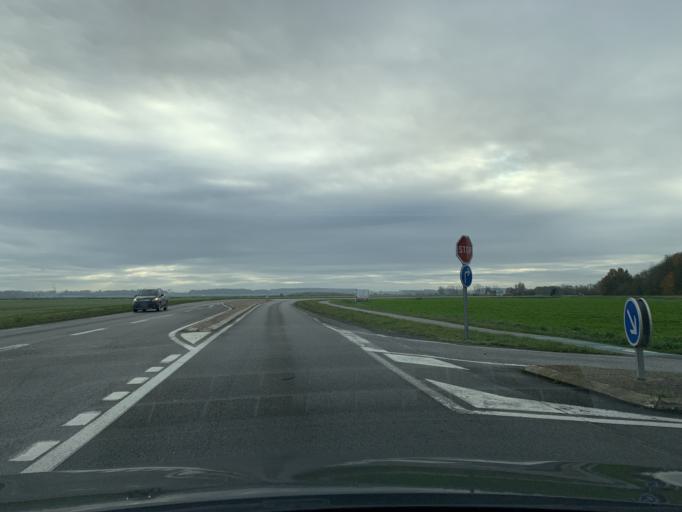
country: FR
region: Nord-Pas-de-Calais
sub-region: Departement du Nord
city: Goeulzin
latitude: 50.3300
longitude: 3.1073
